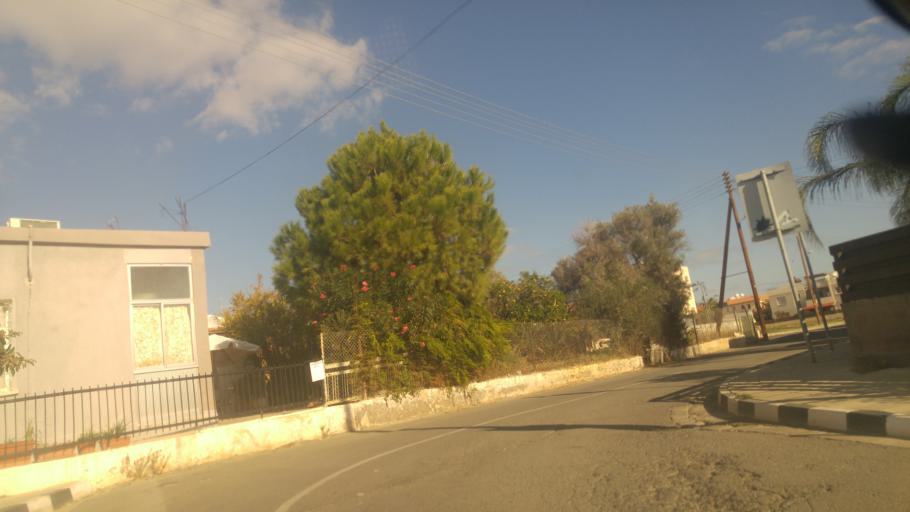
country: CY
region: Limassol
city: Ypsonas
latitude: 34.6869
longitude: 32.9642
